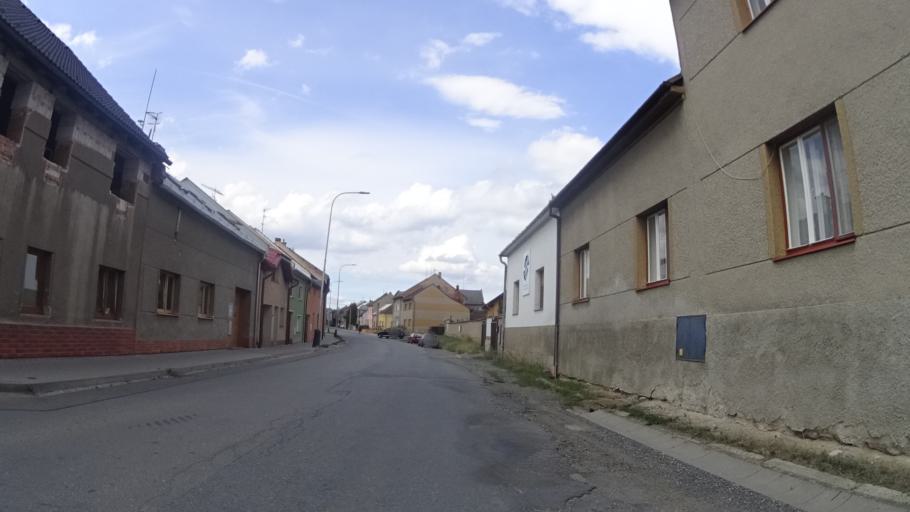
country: CZ
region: Olomoucky
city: Horka nad Moravou
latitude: 49.6374
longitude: 17.2063
